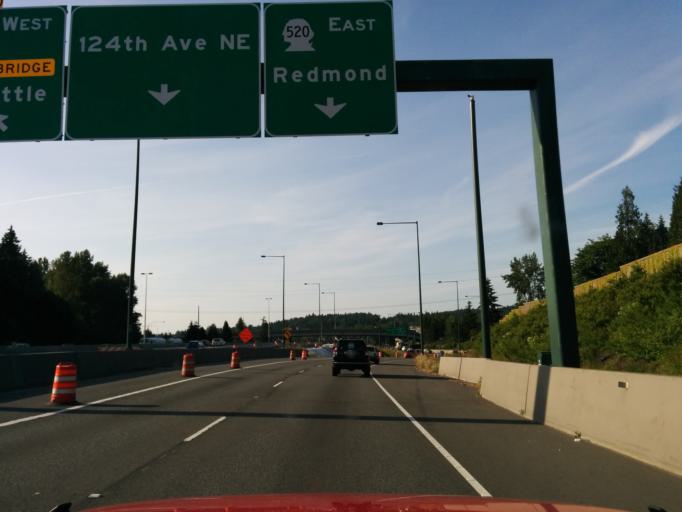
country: US
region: Washington
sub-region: King County
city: Bellevue
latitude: 47.6280
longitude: -122.1880
